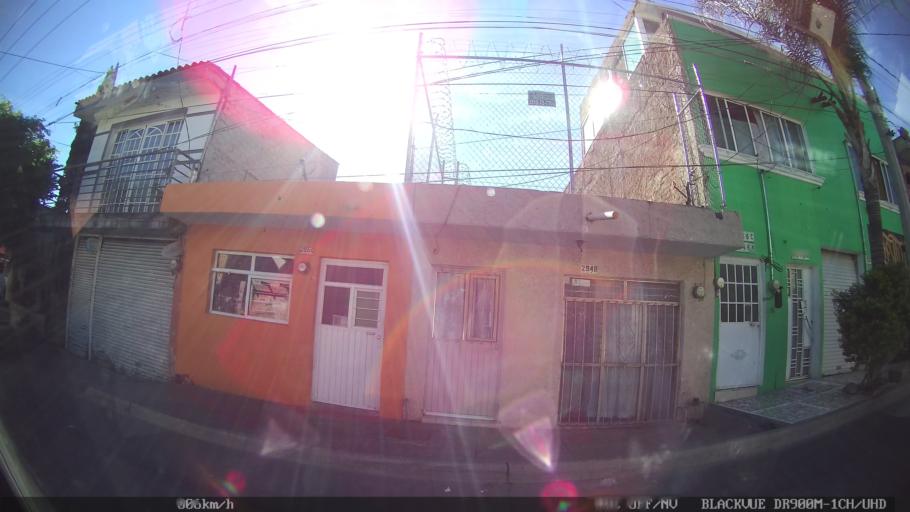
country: MX
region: Jalisco
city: Tlaquepaque
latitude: 20.6944
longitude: -103.2777
